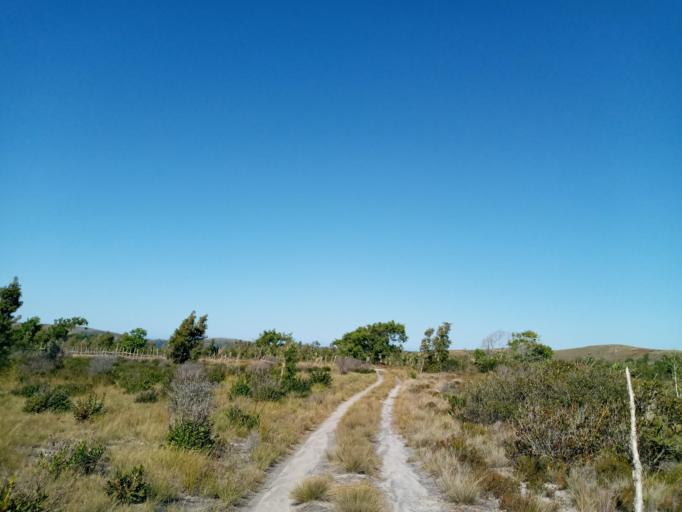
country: MG
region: Anosy
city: Fort Dauphin
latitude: -24.9069
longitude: 47.0944
